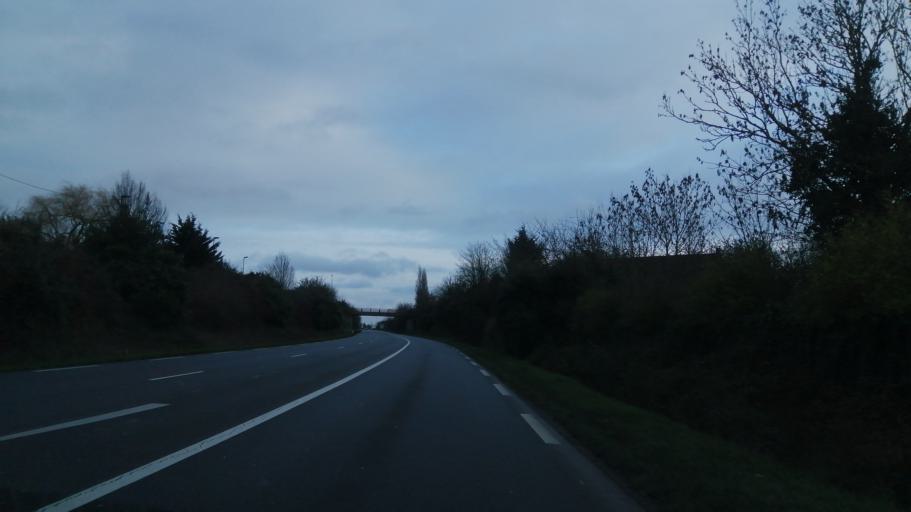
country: FR
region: Nord-Pas-de-Calais
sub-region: Departement du Pas-de-Calais
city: Rouvroy
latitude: 50.3966
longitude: 2.9006
